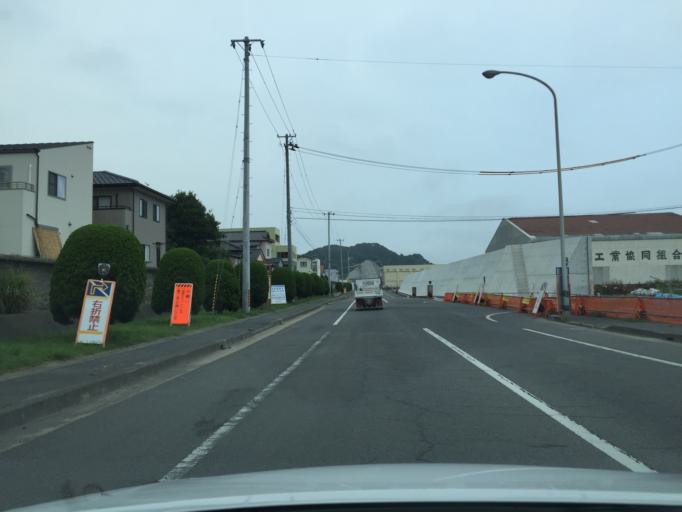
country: JP
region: Fukushima
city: Iwaki
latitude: 36.9561
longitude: 140.9481
